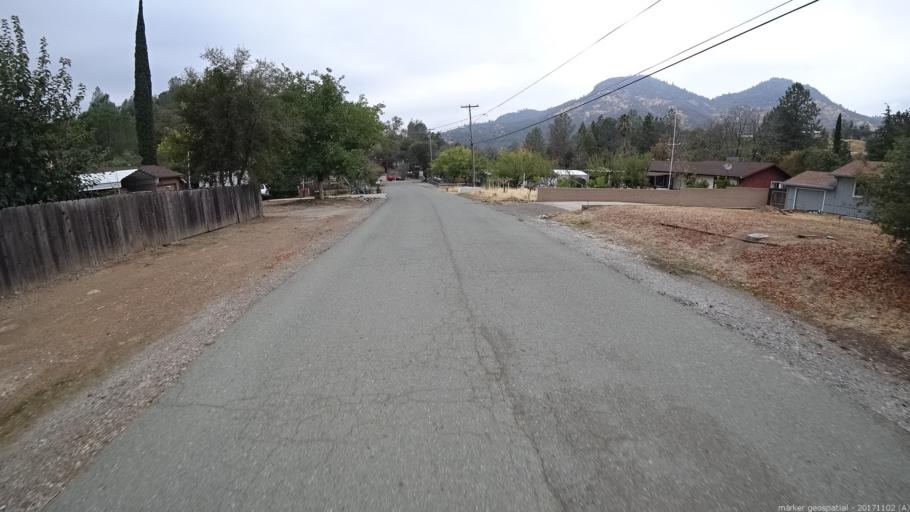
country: US
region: California
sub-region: Shasta County
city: Bella Vista
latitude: 40.7178
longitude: -122.2348
